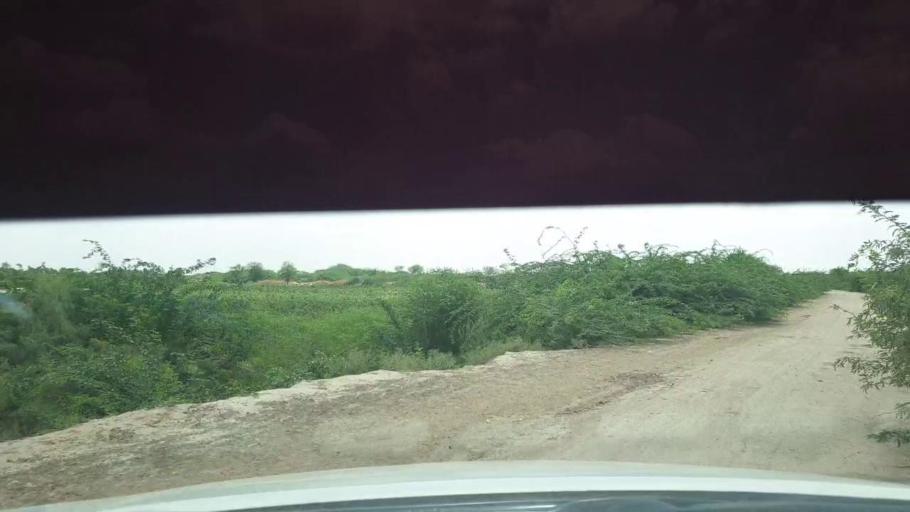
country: PK
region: Sindh
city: Kadhan
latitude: 24.5250
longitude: 69.0867
